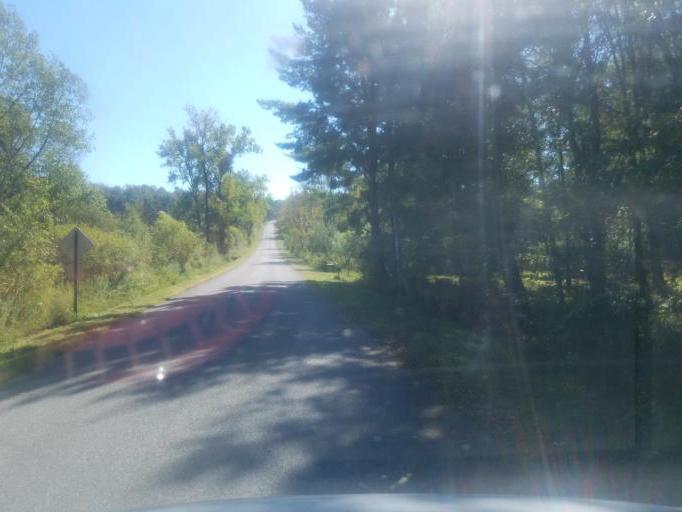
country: US
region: New York
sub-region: Allegany County
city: Houghton
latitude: 42.3212
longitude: -78.2068
